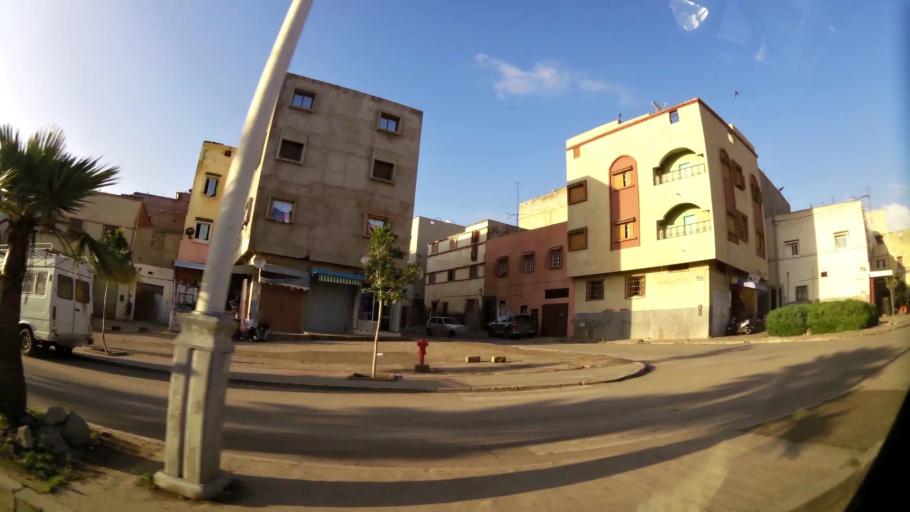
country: MA
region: Chaouia-Ouardigha
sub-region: Settat Province
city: Settat
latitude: 33.0002
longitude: -7.6101
